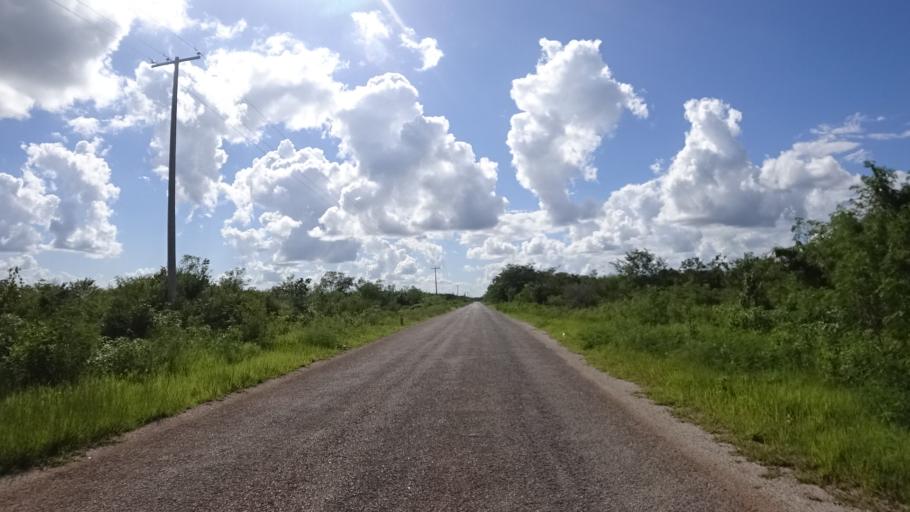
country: MX
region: Yucatan
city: Muna
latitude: 20.6472
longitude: -89.6940
